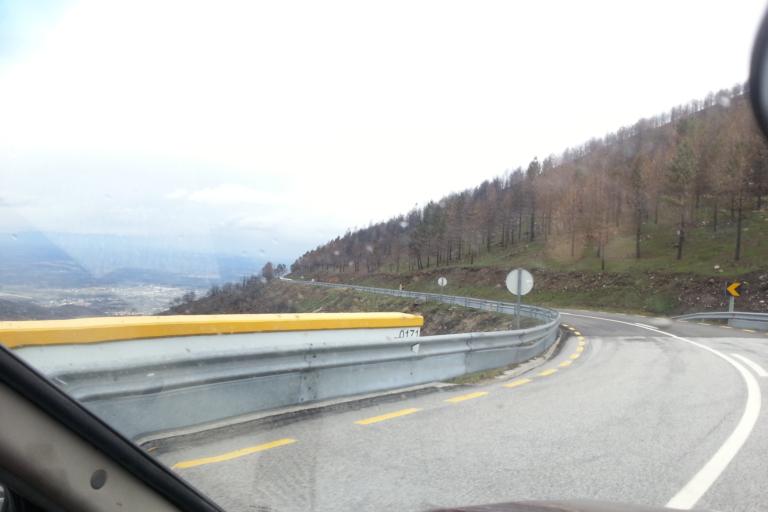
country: PT
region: Guarda
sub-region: Manteigas
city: Manteigas
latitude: 40.4410
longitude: -7.5963
